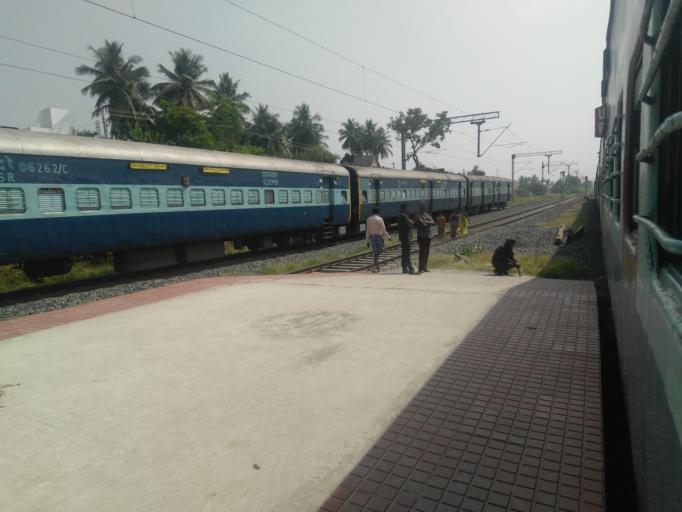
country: IN
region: Tamil Nadu
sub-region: Coimbatore
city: Mettupalayam
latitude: 11.2943
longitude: 76.9366
